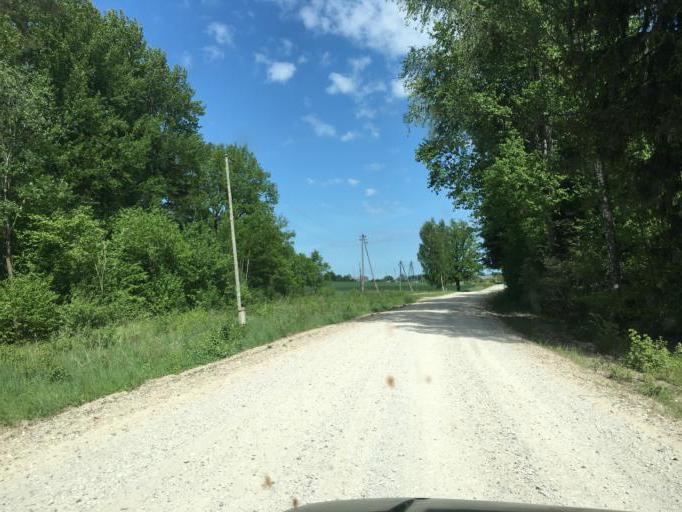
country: LV
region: Talsu Rajons
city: Valdemarpils
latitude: 57.3683
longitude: 22.6213
